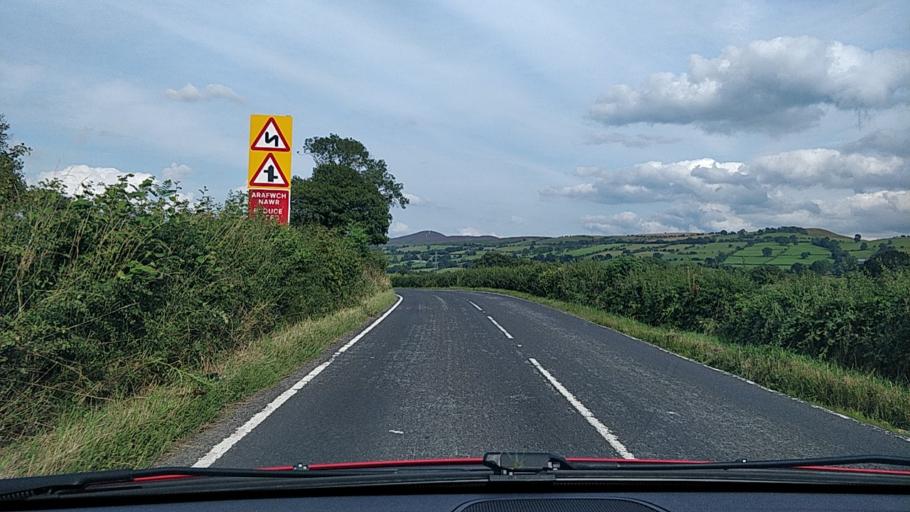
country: GB
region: Wales
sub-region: Denbighshire
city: Corwen
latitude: 53.0002
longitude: -3.3427
